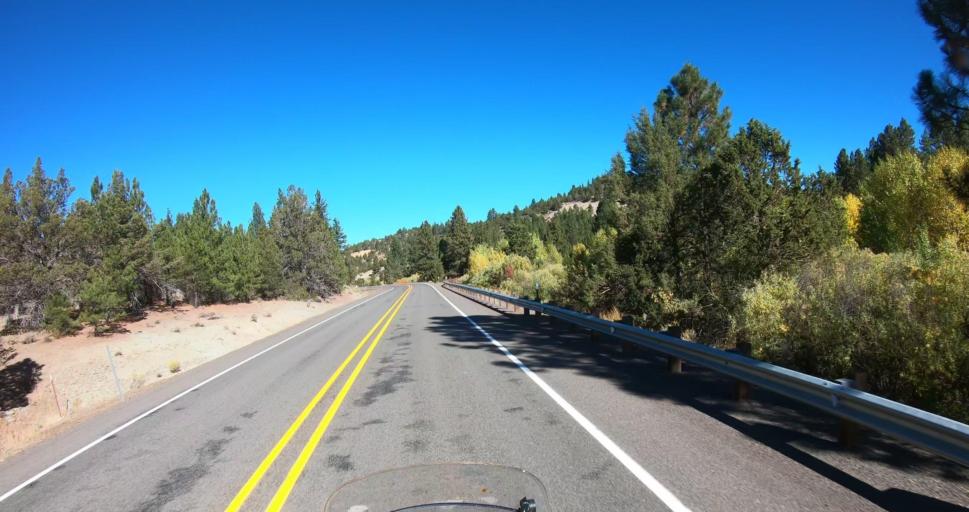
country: US
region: Oregon
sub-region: Lake County
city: Lakeview
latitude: 42.2570
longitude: -120.3336
